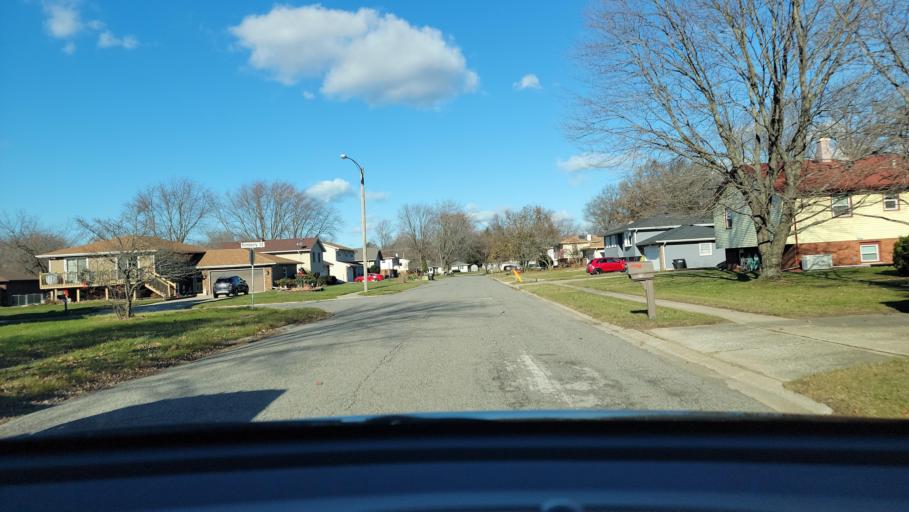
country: US
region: Indiana
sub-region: Porter County
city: Portage
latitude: 41.5631
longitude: -87.1870
